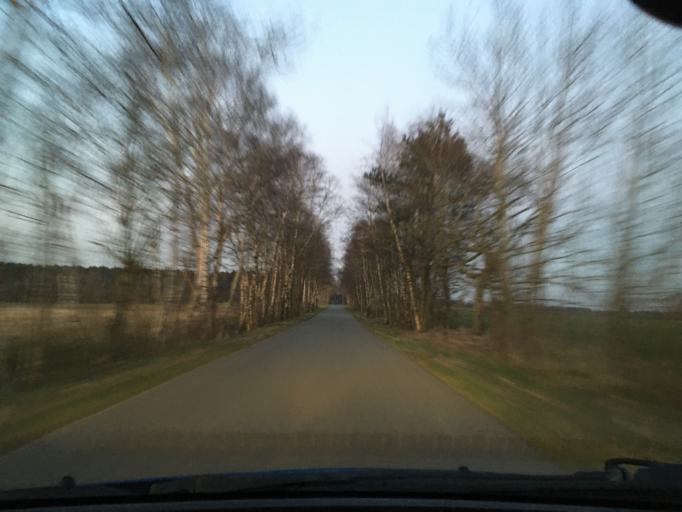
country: DE
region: Lower Saxony
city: Rehlingen
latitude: 53.0678
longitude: 10.2577
